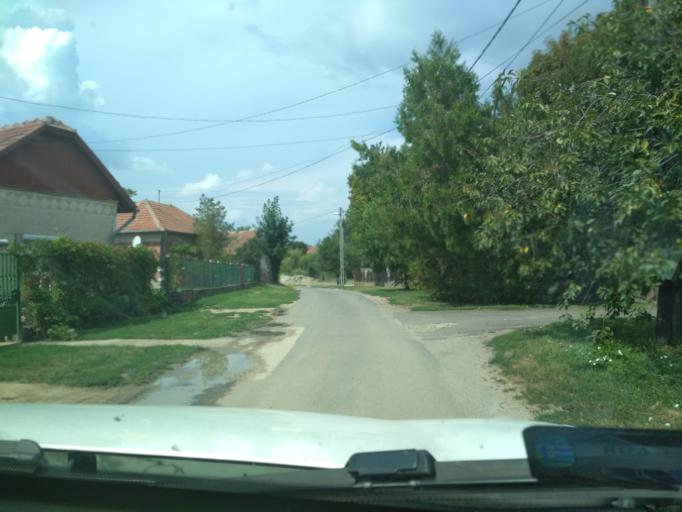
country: HU
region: Jasz-Nagykun-Szolnok
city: Abadszalok
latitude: 47.4746
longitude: 20.5863
